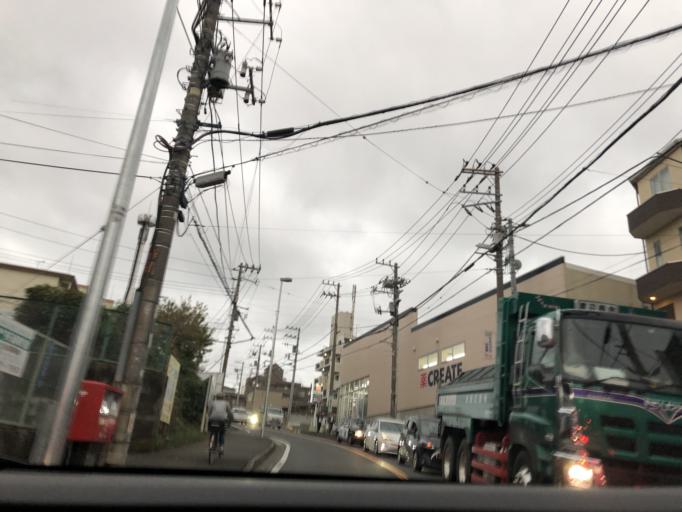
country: JP
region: Kanagawa
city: Yokohama
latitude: 35.5166
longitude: 139.6477
